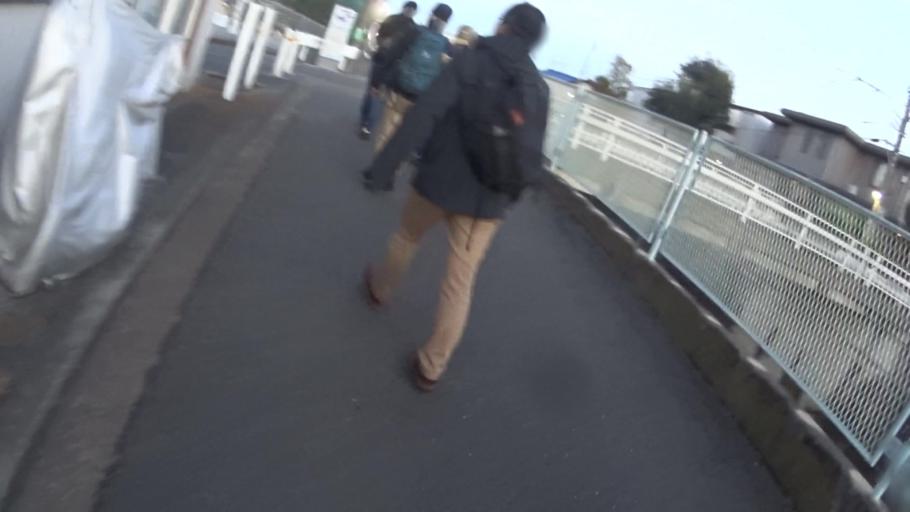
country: JP
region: Tokyo
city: Chofugaoka
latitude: 35.6320
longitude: 139.5317
